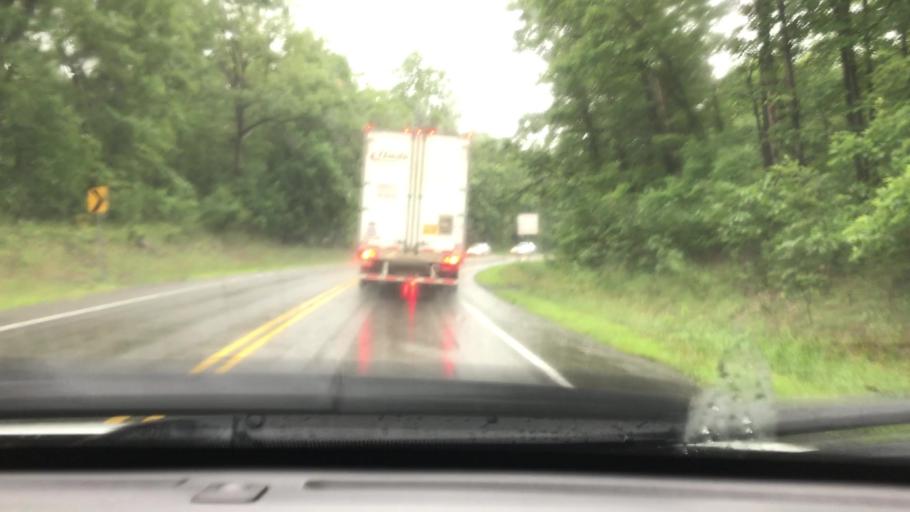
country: US
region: Pennsylvania
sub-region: Clearfield County
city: Osceola Mills
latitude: 40.7819
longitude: -78.2401
